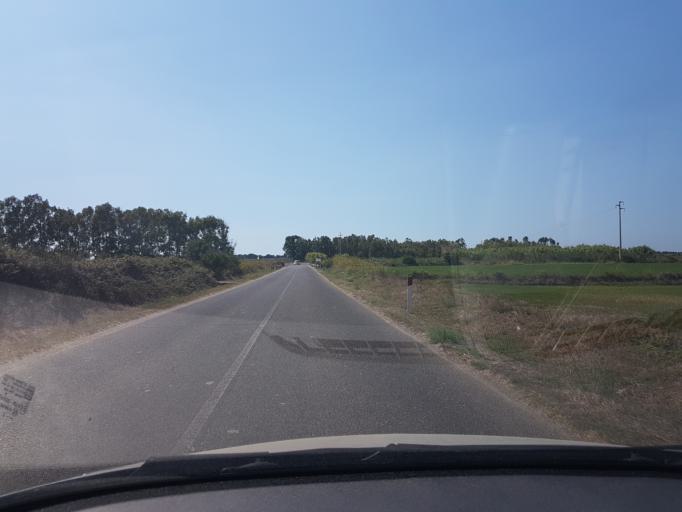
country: IT
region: Sardinia
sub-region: Provincia di Oristano
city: Riola Sardo
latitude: 40.0005
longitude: 8.5065
